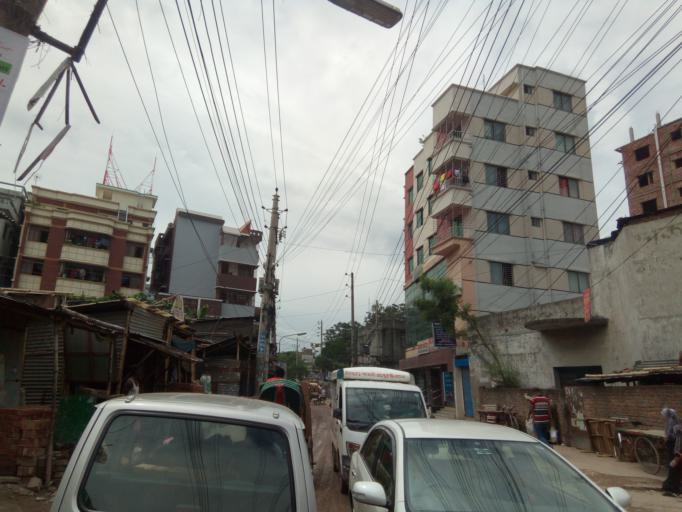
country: BD
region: Dhaka
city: Azimpur
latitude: 23.7605
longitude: 90.3588
